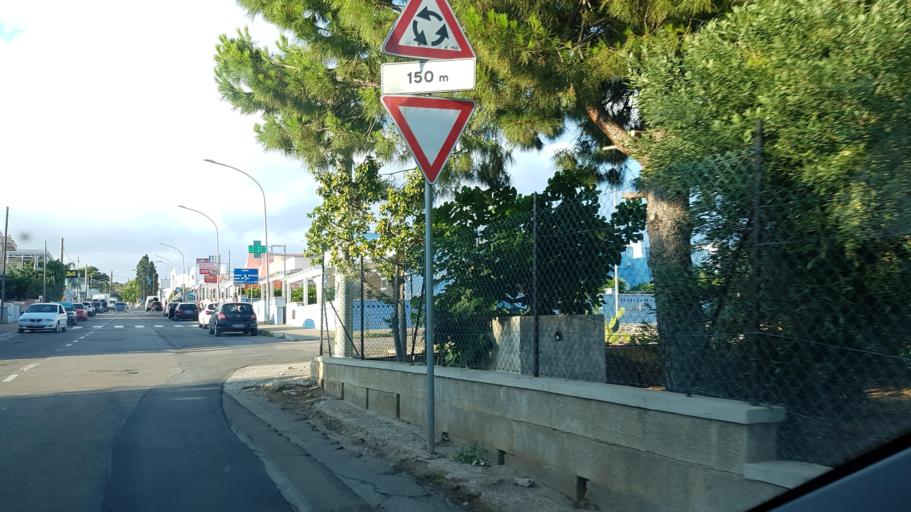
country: IT
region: Apulia
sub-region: Provincia di Lecce
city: Gemini
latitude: 39.8427
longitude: 18.2096
